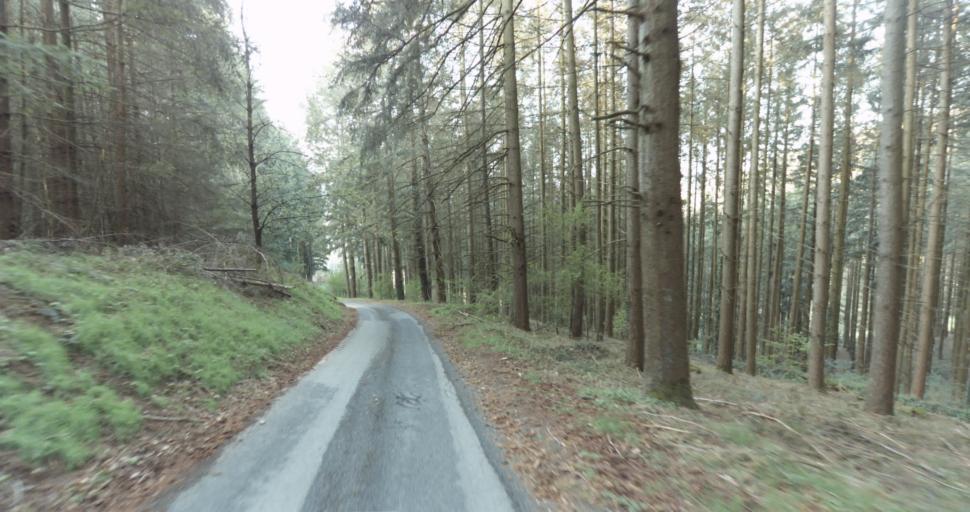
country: FR
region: Rhone-Alpes
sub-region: Departement du Rhone
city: Tarare
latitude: 45.9009
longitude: 4.4211
